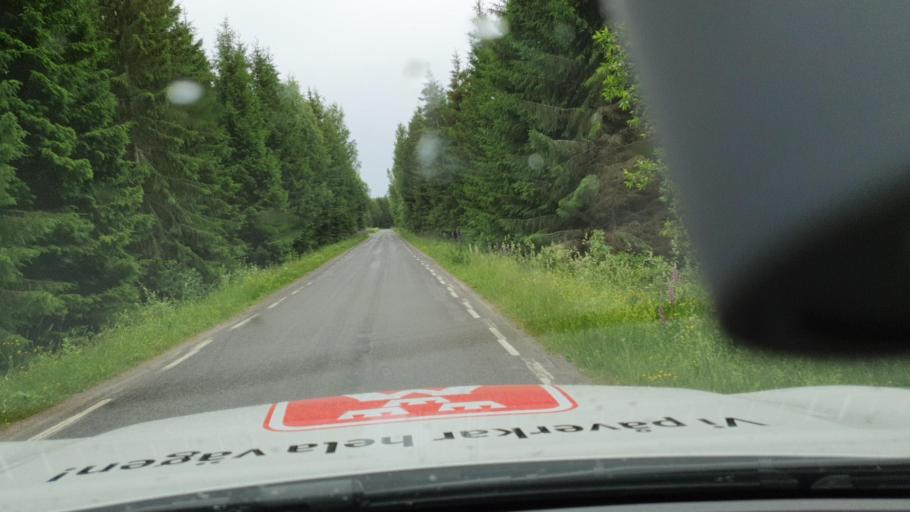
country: SE
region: Vaestra Goetaland
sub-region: Tibro Kommun
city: Tibro
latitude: 58.3231
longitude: 14.1839
